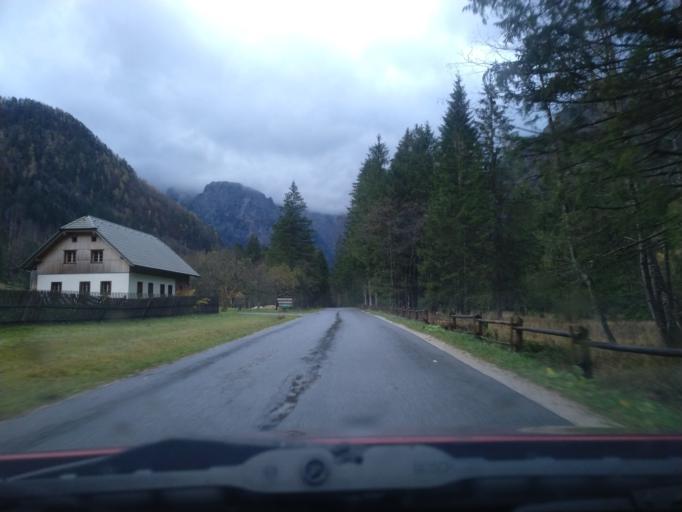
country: SI
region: Solcava
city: Solcava
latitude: 46.4085
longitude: 14.6365
